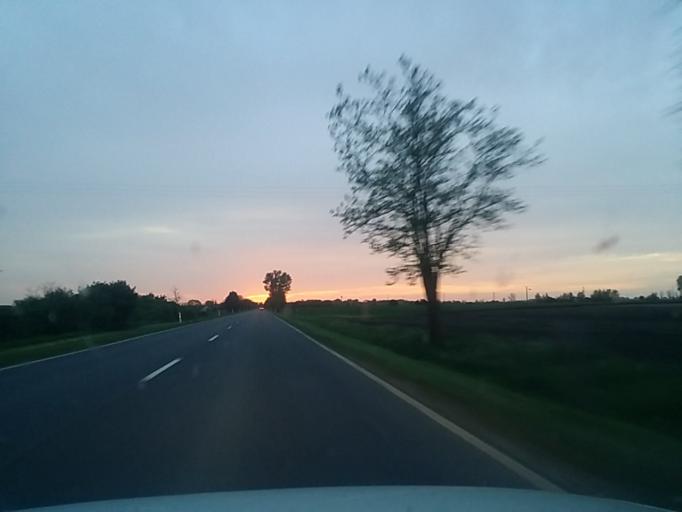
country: HU
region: Bekes
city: Kondoros
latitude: 46.7461
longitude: 20.8555
